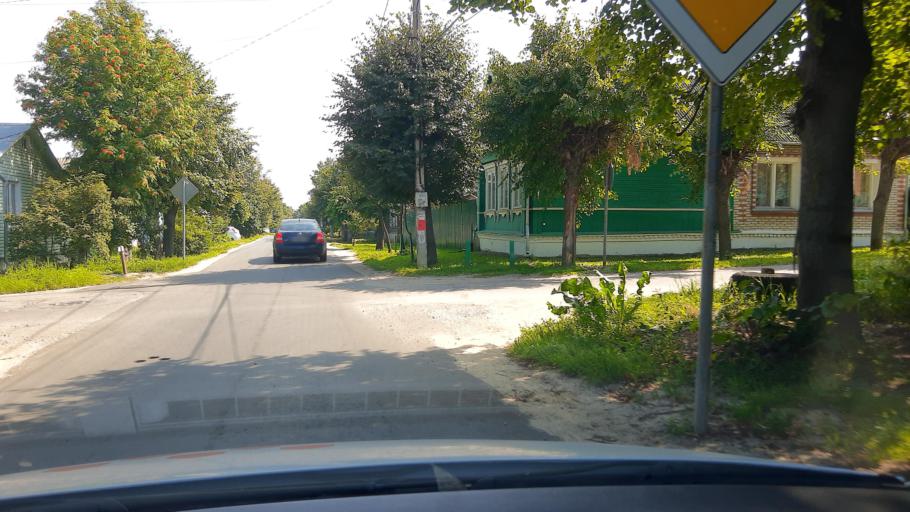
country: RU
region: Moskovskaya
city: Bronnitsy
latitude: 55.4255
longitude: 38.2571
